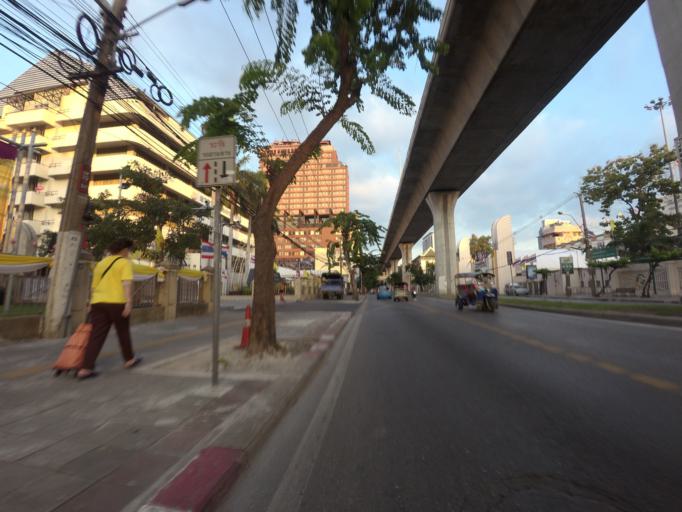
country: TH
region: Bangkok
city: Pathum Wan
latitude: 13.7472
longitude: 100.5255
